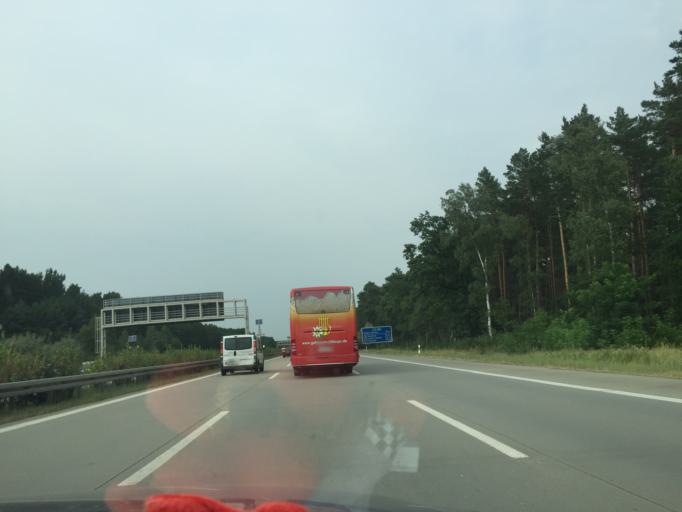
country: DE
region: Brandenburg
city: Erkner
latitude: 52.3369
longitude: 13.7531
